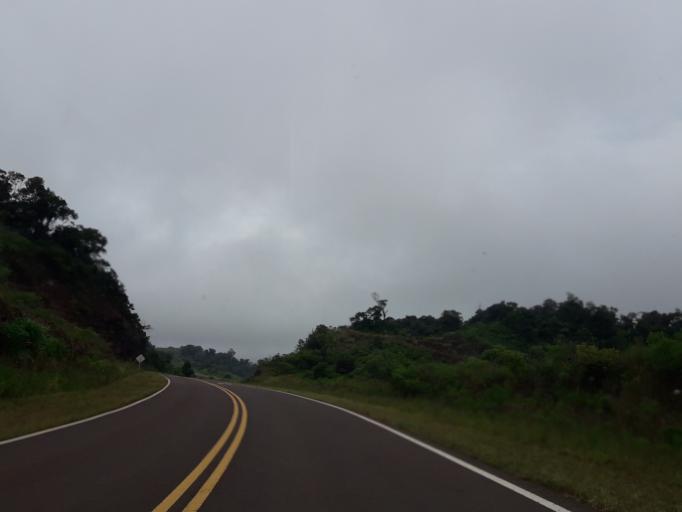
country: AR
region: Misiones
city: Bernardo de Irigoyen
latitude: -26.4002
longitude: -53.8183
